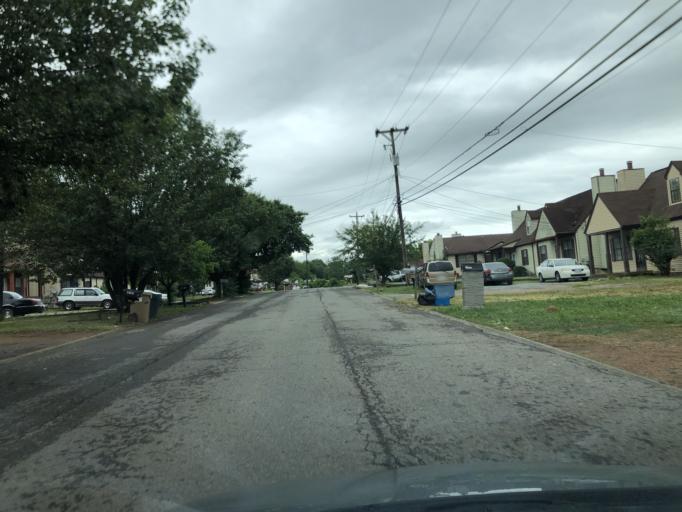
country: US
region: Tennessee
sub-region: Davidson County
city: Nashville
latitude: 36.2459
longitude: -86.7781
